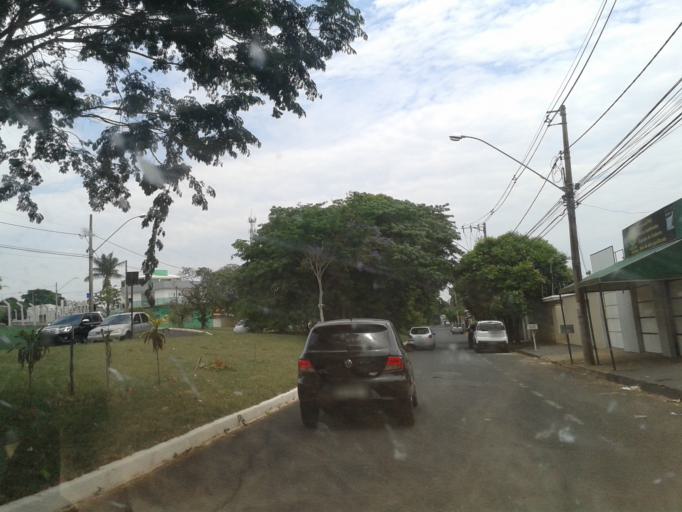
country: BR
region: Minas Gerais
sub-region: Uberlandia
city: Uberlandia
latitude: -18.9227
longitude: -48.3068
